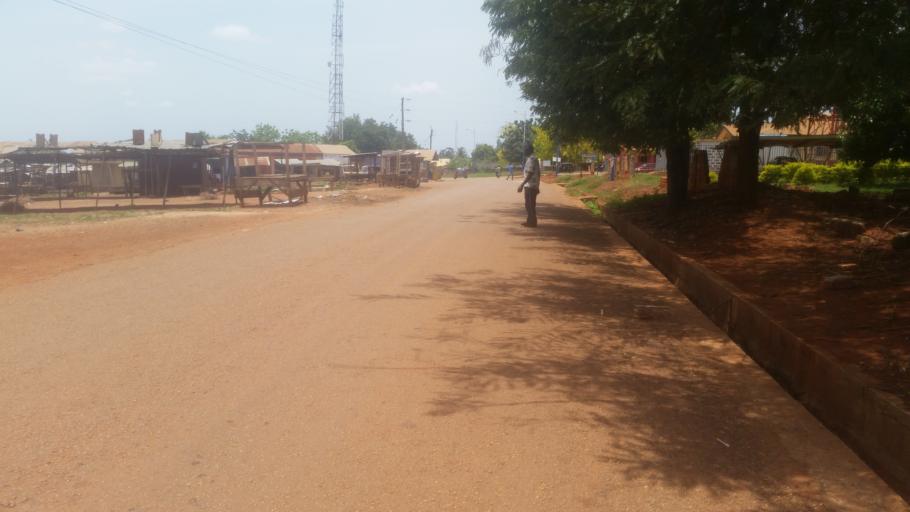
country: GH
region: Western
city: Bibiani
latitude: 6.8074
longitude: -2.5177
